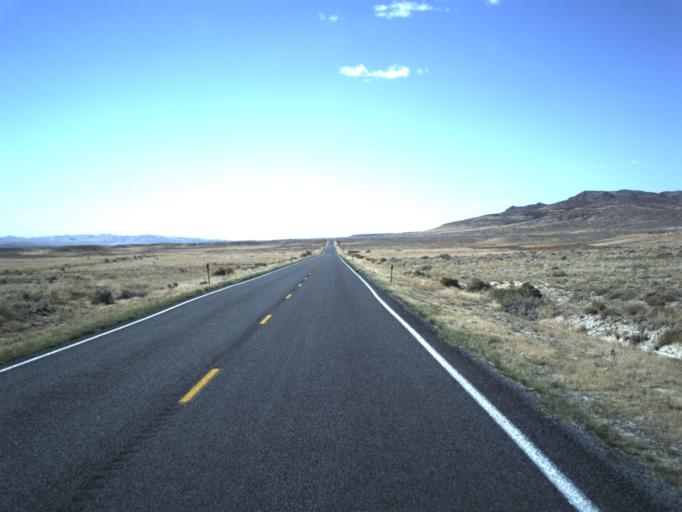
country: US
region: Utah
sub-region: Millard County
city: Fillmore
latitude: 38.9010
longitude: -112.8219
